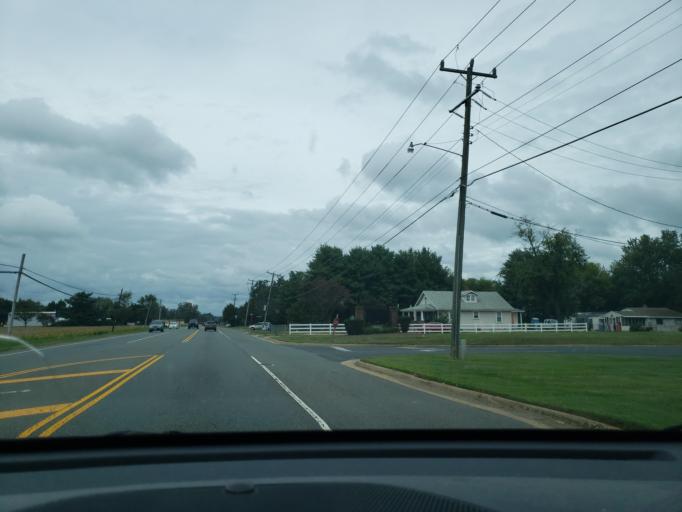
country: US
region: Virginia
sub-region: City of Fredericksburg
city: Fredericksburg
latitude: 38.2669
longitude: -77.4421
